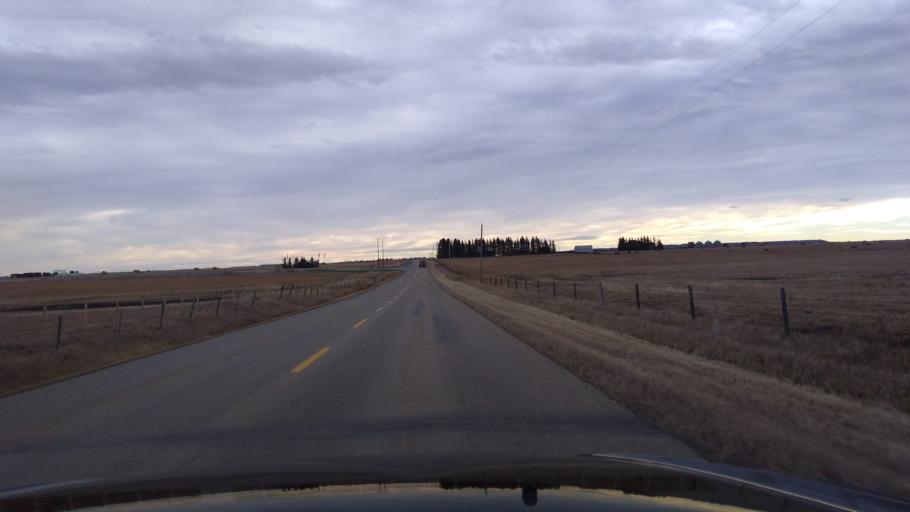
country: CA
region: Alberta
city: Cochrane
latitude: 51.0960
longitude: -114.3928
